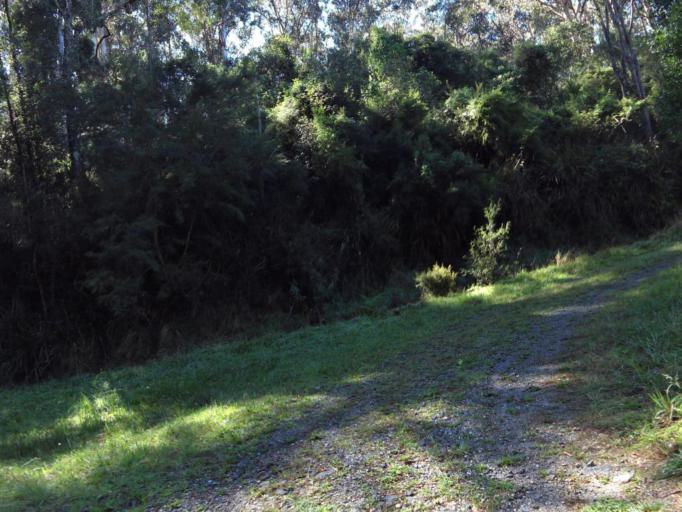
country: AU
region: Victoria
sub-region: Yarra Ranges
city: Launching Place
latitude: -37.7399
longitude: 145.5701
